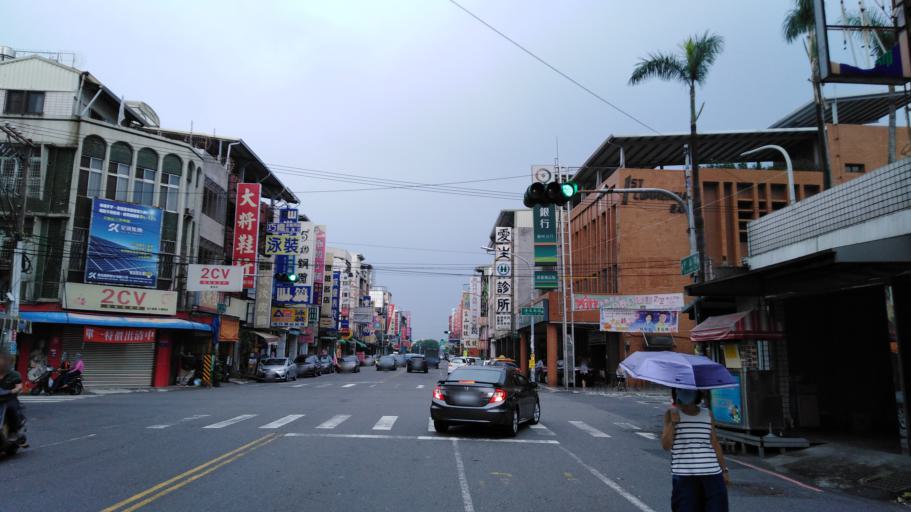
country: TW
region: Taiwan
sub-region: Pingtung
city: Pingtung
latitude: 22.5496
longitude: 120.5399
